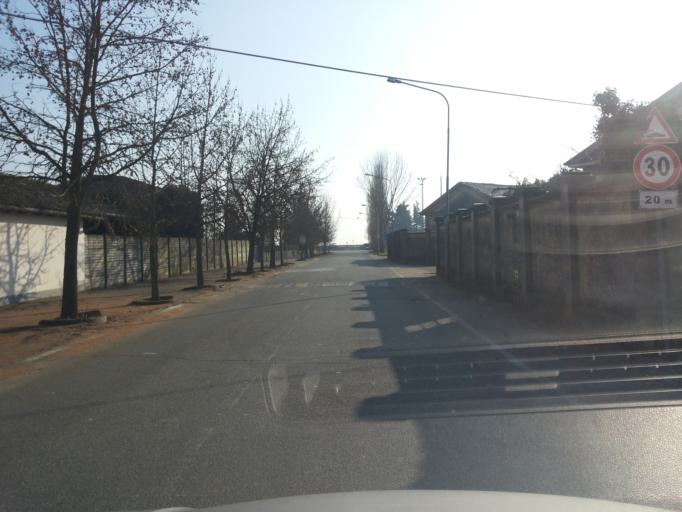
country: IT
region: Piedmont
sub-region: Provincia di Vercelli
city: Stroppiana
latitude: 45.2298
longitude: 8.4601
